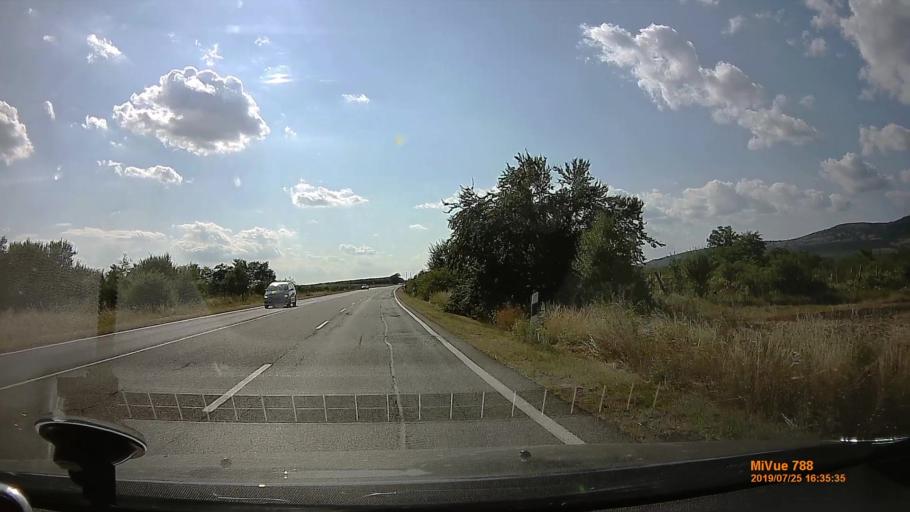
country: HU
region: Heves
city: Abasar
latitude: 47.7672
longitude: 20.0004
